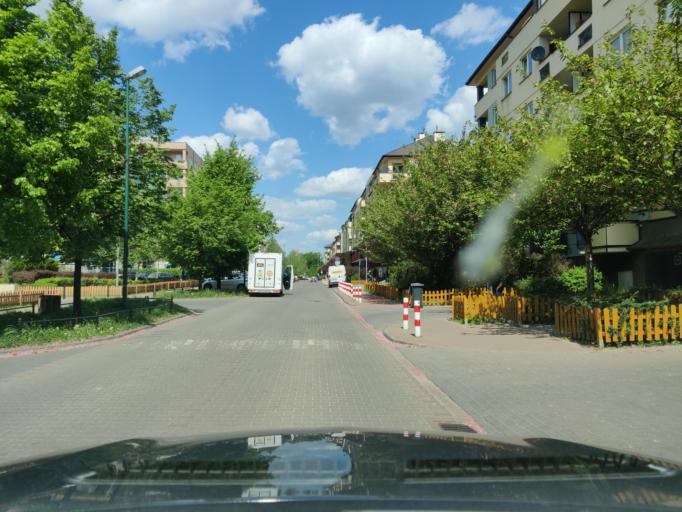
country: PL
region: Masovian Voivodeship
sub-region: Warszawa
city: Kabaty
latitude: 52.1319
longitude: 21.0673
